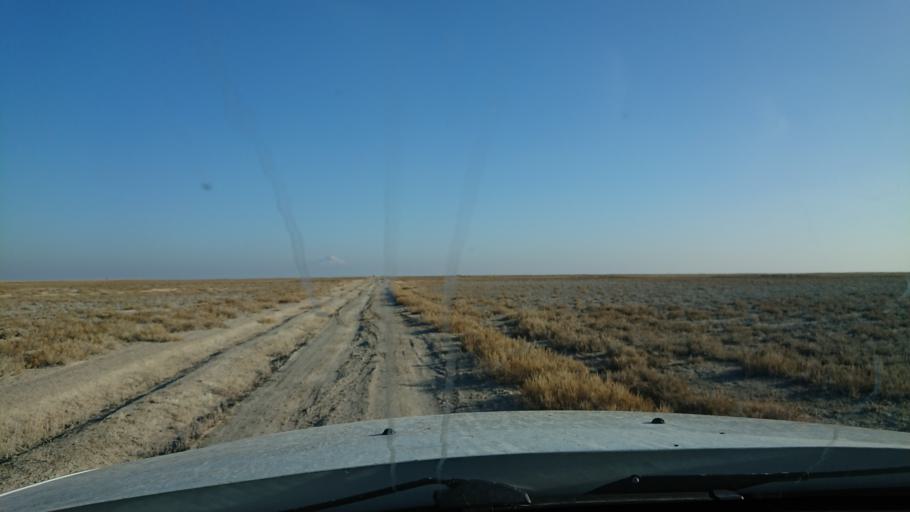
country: TR
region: Aksaray
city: Eskil
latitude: 38.4064
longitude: 33.5707
